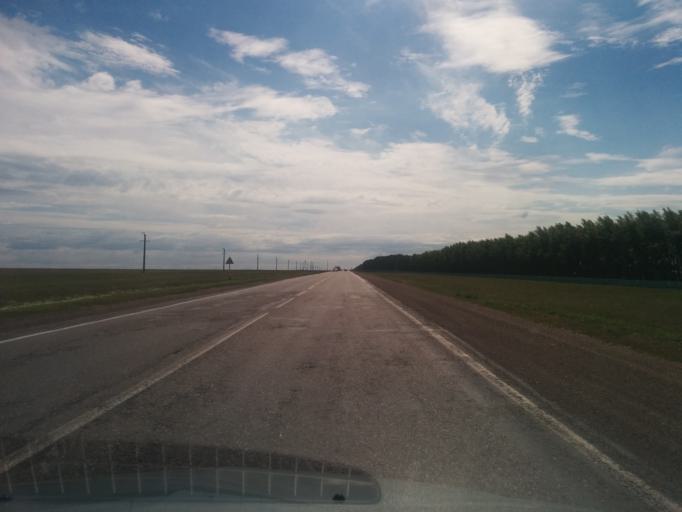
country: RU
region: Bashkortostan
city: Karmaskaly
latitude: 54.4236
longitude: 56.0372
